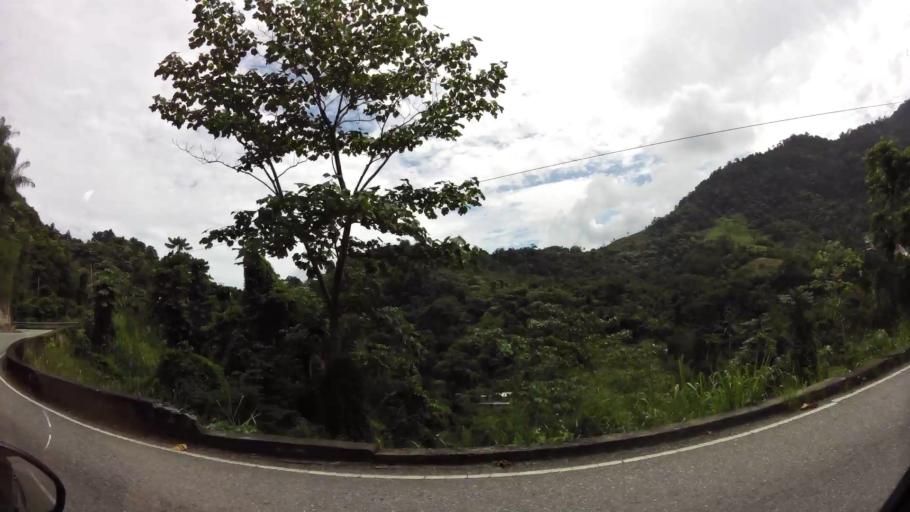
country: TT
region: Diego Martin
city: Petit Valley
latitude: 10.7160
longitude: -61.5326
